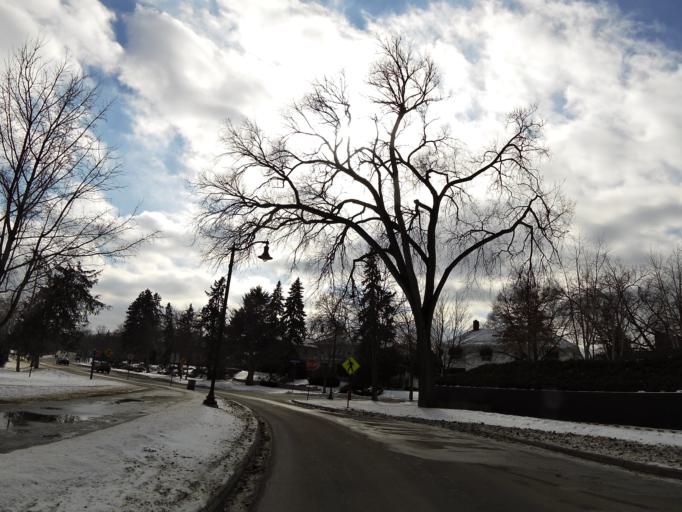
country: US
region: Minnesota
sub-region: Hennepin County
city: Saint Louis Park
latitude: 44.9575
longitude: -93.3126
